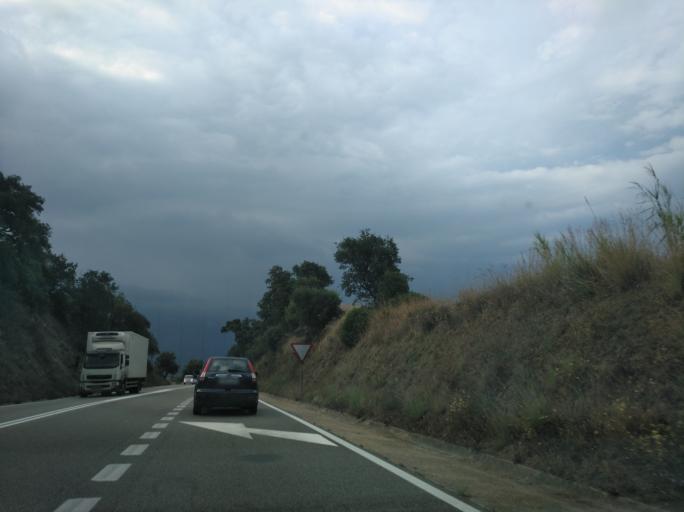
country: ES
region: Catalonia
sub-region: Provincia de Barcelona
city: Tordera
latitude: 41.6872
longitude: 2.7221
